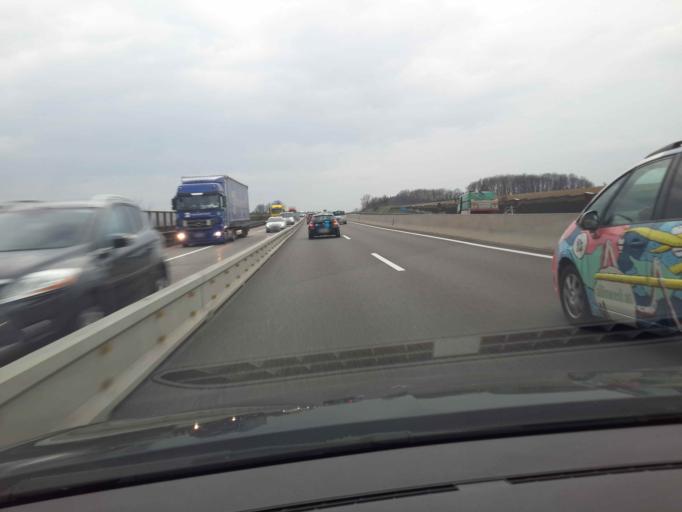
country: AT
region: Lower Austria
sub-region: Politischer Bezirk Sankt Polten
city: Boheimkirchen
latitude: 48.1862
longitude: 15.7234
